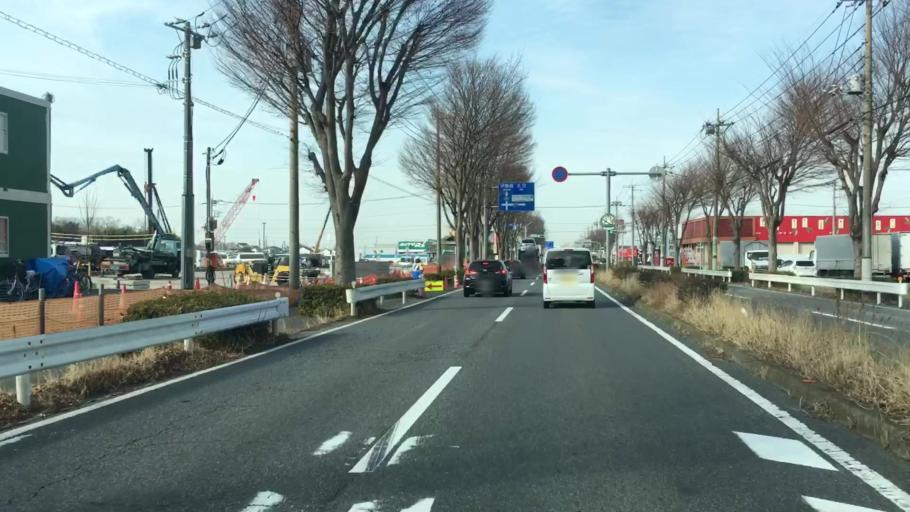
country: JP
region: Gunma
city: Tatebayashi
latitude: 36.2318
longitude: 139.5531
